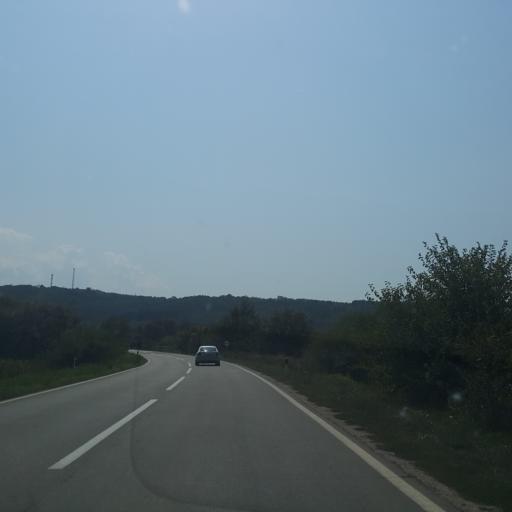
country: RS
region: Central Serbia
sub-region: Zajecarski Okrug
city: Zajecar
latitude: 43.7997
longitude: 22.2989
